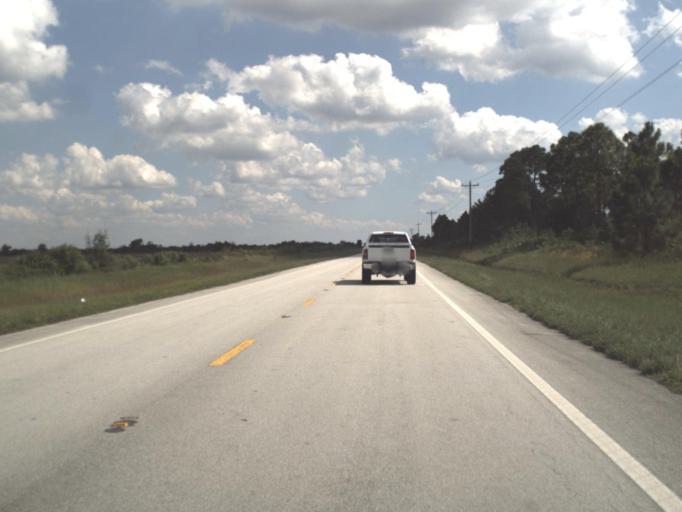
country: US
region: Florida
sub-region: Highlands County
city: Lake Placid
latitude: 27.4358
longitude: -81.2353
